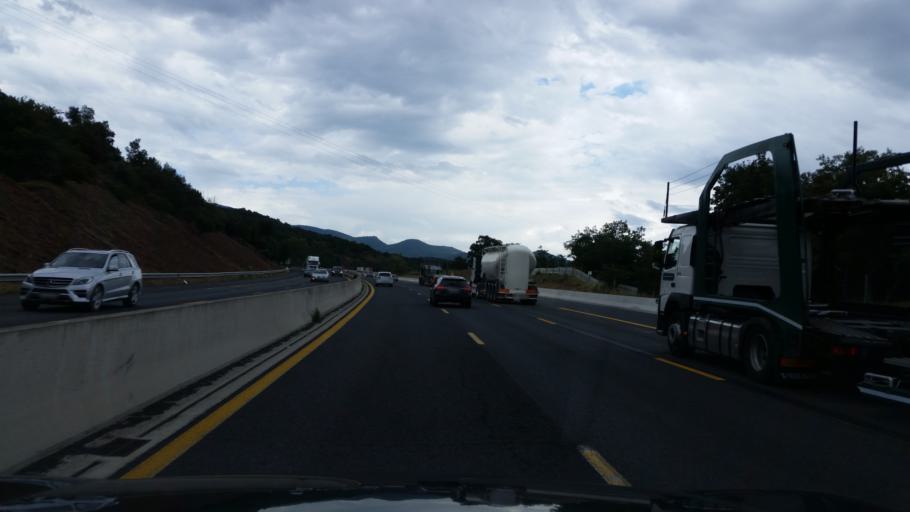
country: FR
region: Languedoc-Roussillon
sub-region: Departement des Pyrenees-Orientales
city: Maureillas-las-Illas
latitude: 42.4973
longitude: 2.8235
